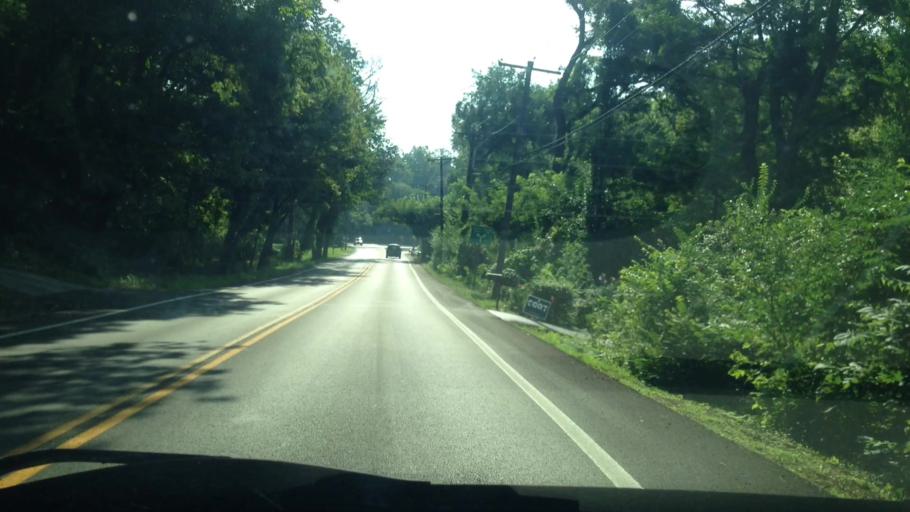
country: US
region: Missouri
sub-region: Saint Louis County
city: Des Peres
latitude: 38.5803
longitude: -90.4422
